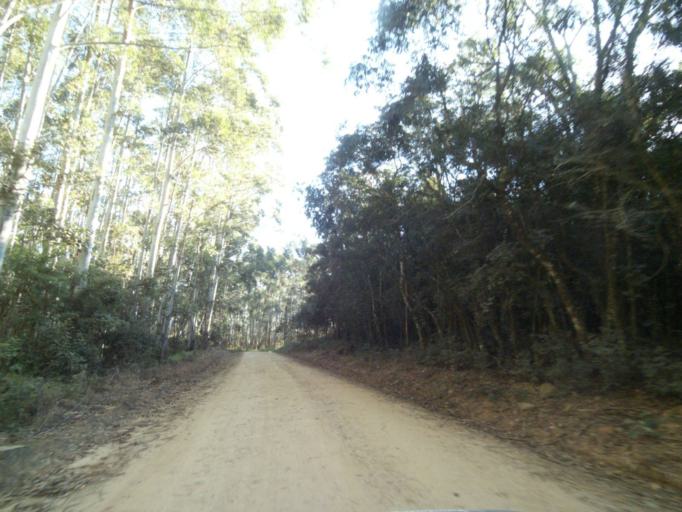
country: BR
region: Parana
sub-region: Telemaco Borba
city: Telemaco Borba
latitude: -24.5112
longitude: -50.6578
